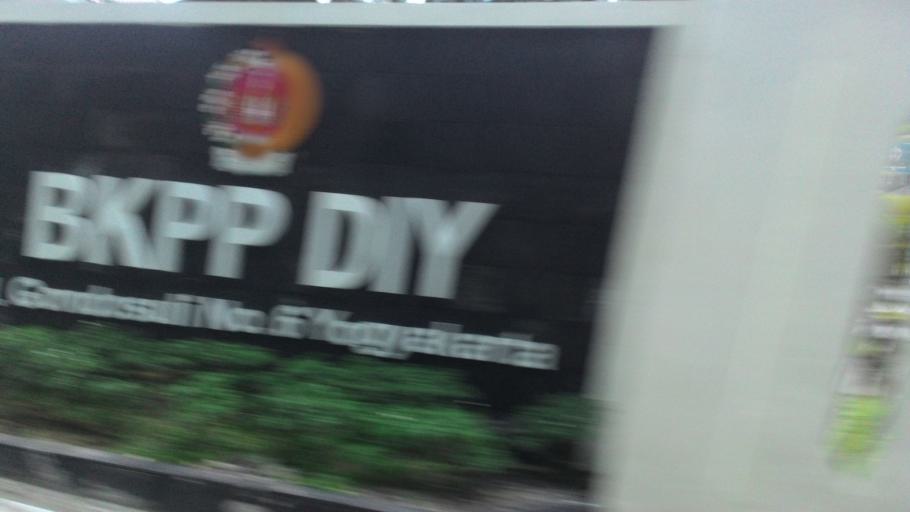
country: ID
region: Daerah Istimewa Yogyakarta
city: Yogyakarta
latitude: -7.7955
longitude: 110.3854
